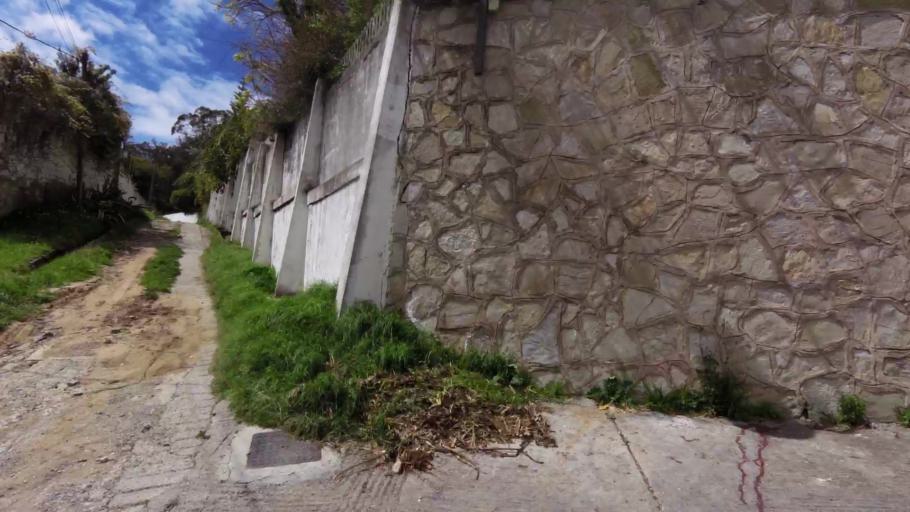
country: MA
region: Tanger-Tetouan
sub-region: Tanger-Assilah
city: Tangier
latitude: 35.7875
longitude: -5.8516
